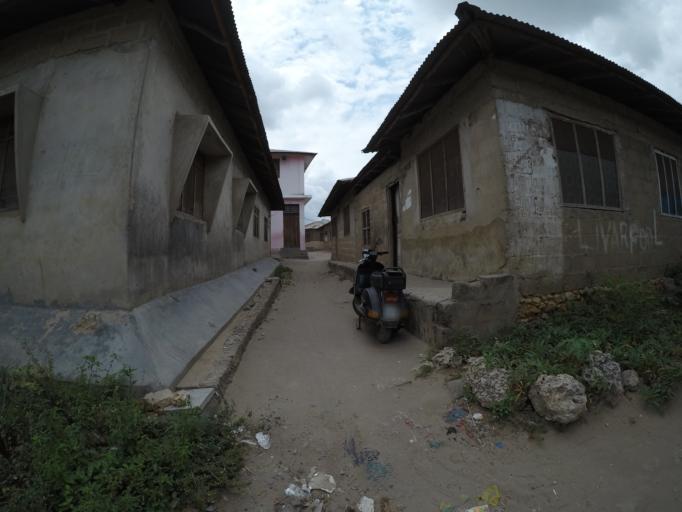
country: TZ
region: Zanzibar Urban/West
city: Zanzibar
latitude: -6.1813
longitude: 39.2093
